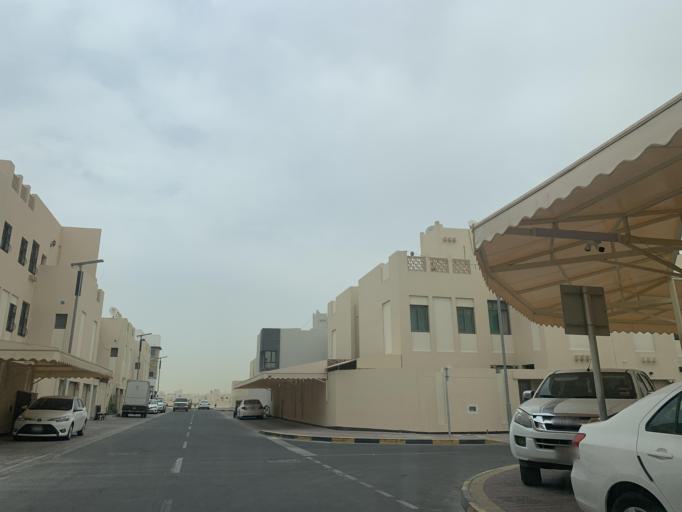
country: BH
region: Northern
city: Madinat `Isa
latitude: 26.1705
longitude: 50.5147
